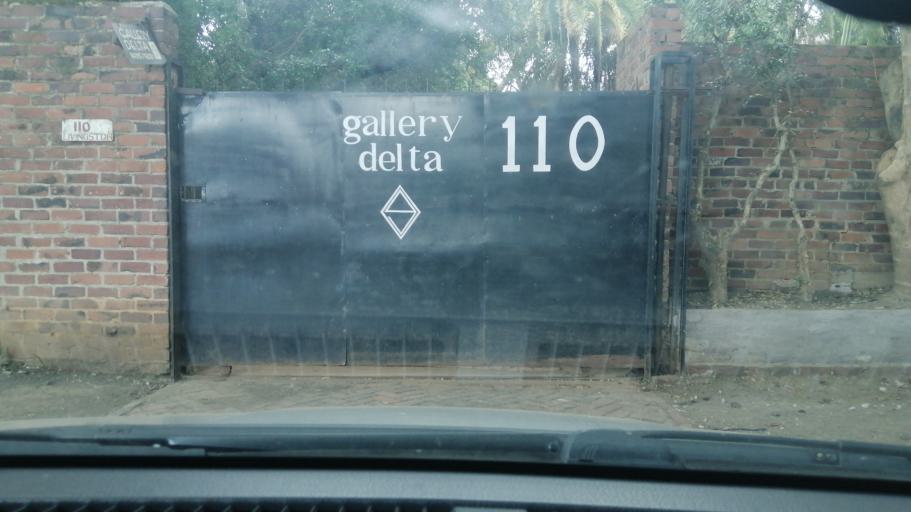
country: ZW
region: Harare
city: Harare
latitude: -17.8199
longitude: 31.0607
